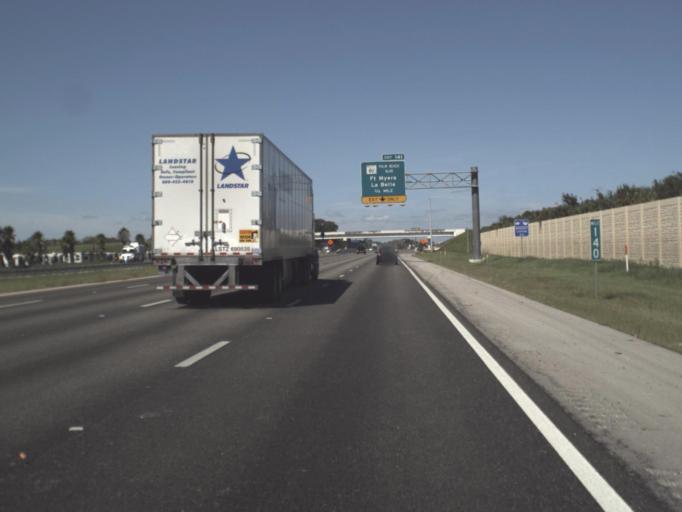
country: US
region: Florida
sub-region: Lee County
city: Tice
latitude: 26.6676
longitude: -81.7995
